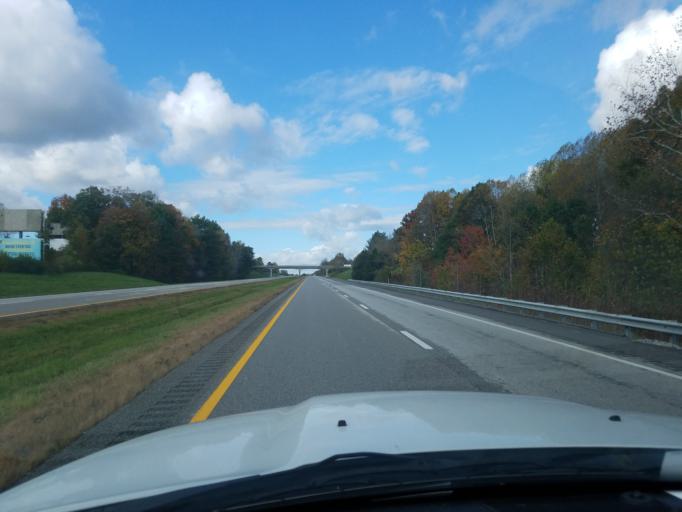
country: US
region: Kentucky
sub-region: Russell County
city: Russell Springs
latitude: 37.0711
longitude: -85.0224
